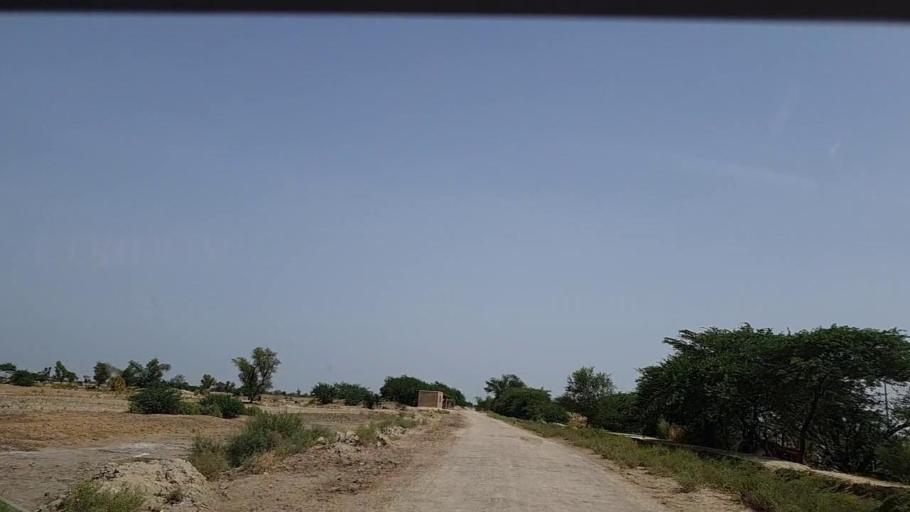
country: PK
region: Sindh
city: Johi
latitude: 26.7744
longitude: 67.6252
